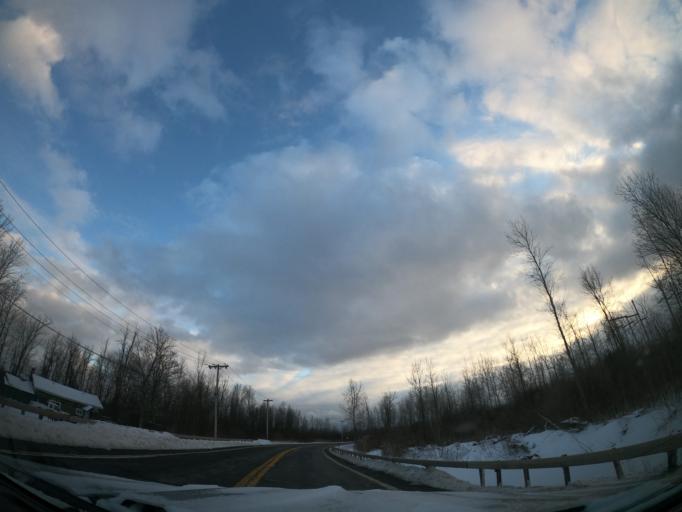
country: US
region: New York
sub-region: Onondaga County
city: Brewerton
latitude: 43.2061
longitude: -76.1663
